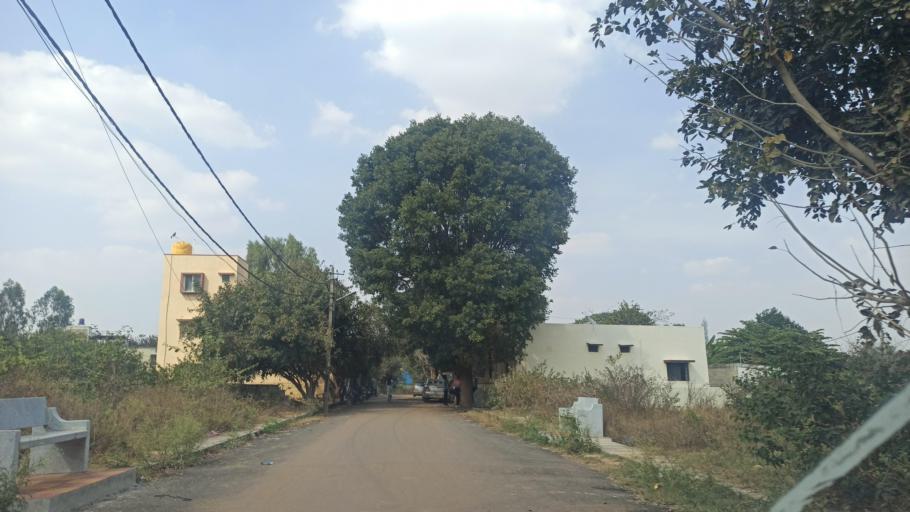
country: IN
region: Karnataka
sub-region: Bangalore Urban
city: Yelahanka
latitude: 13.1149
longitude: 77.6104
